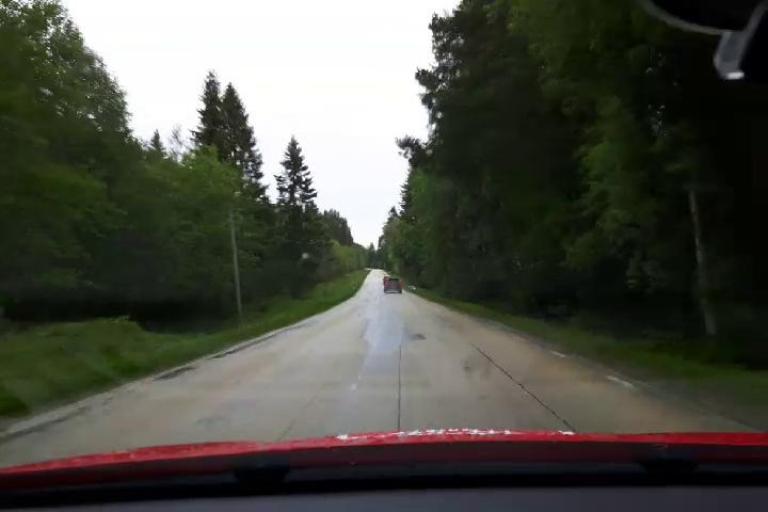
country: SE
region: Jaemtland
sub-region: Bergs Kommun
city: Hoverberg
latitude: 62.7842
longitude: 14.4356
